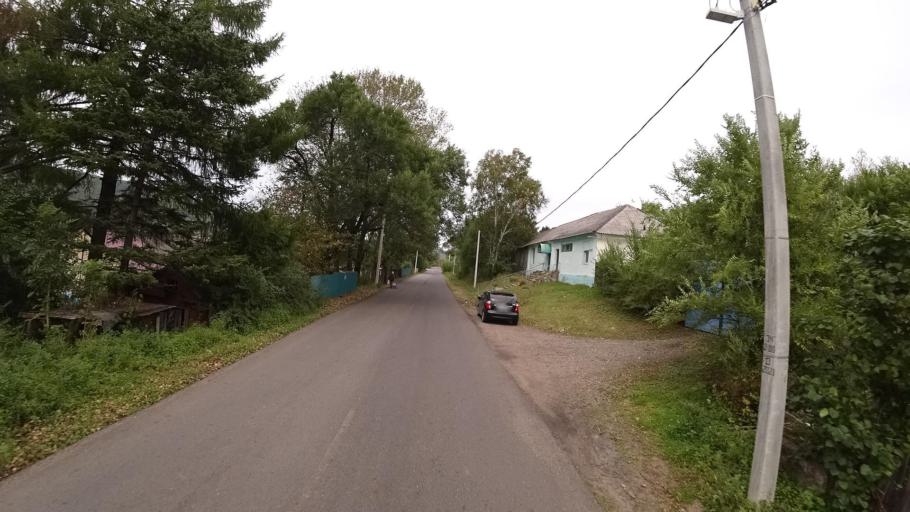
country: RU
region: Jewish Autonomous Oblast
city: Khingansk
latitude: 49.0274
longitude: 131.0587
